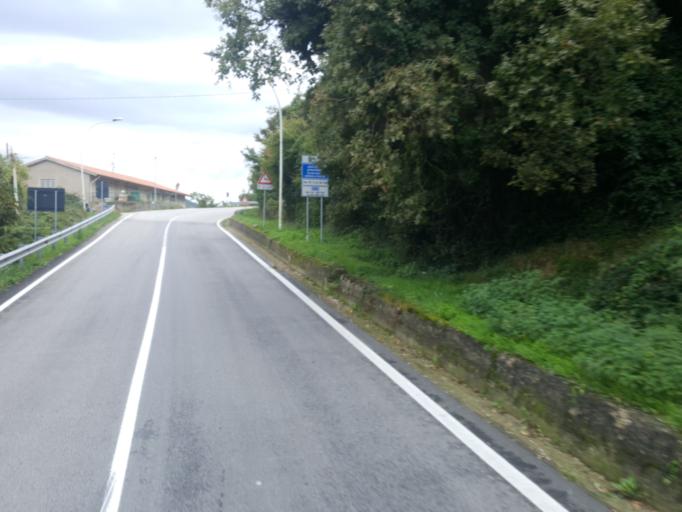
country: IT
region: Tuscany
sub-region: Province of Pisa
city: Castelnuovo di Val di Cecina
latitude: 43.2056
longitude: 10.9053
